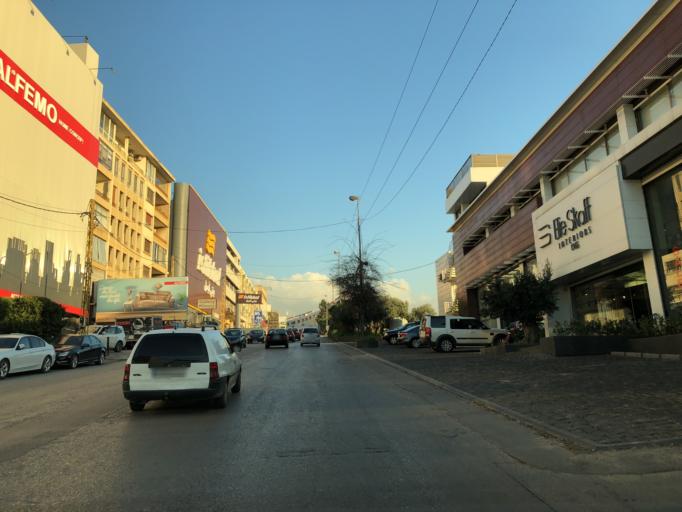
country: LB
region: Mont-Liban
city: Baabda
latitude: 33.8623
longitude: 35.5492
